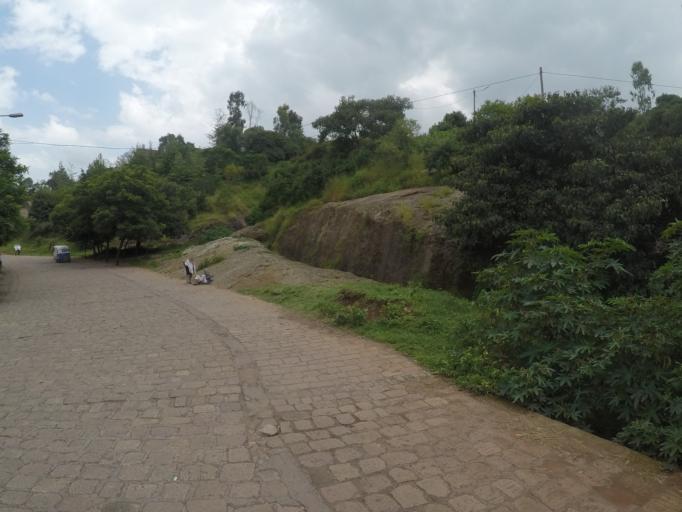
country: ET
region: Amhara
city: Lalibela
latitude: 12.0318
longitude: 39.0435
